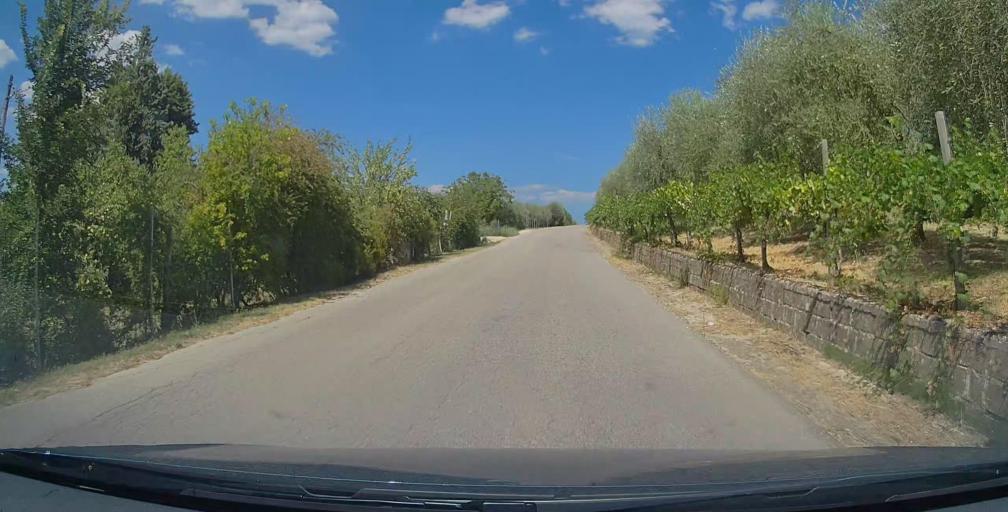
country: IT
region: Umbria
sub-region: Provincia di Terni
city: Otricoli
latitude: 42.4032
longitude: 12.4929
